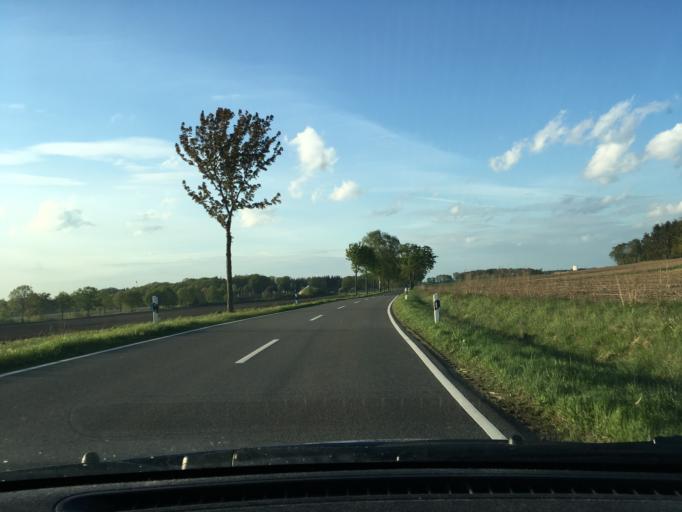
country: DE
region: Lower Saxony
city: Wietzendorf
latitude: 52.8840
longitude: 9.9827
